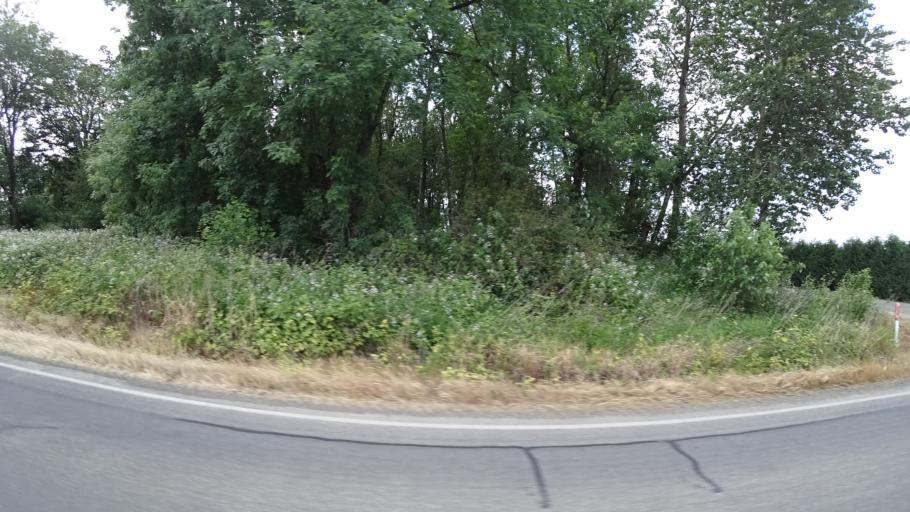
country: US
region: Washington
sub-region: Clark County
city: Felida
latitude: 45.6456
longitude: -122.7797
